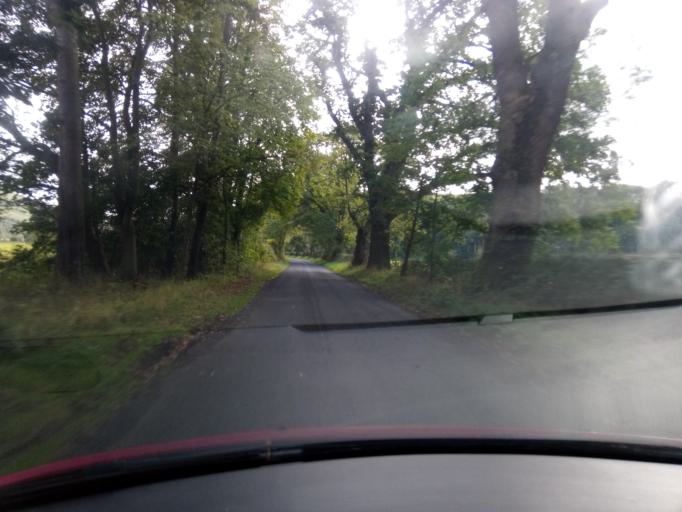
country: GB
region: Scotland
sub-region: The Scottish Borders
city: Kelso
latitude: 55.5085
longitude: -2.3514
